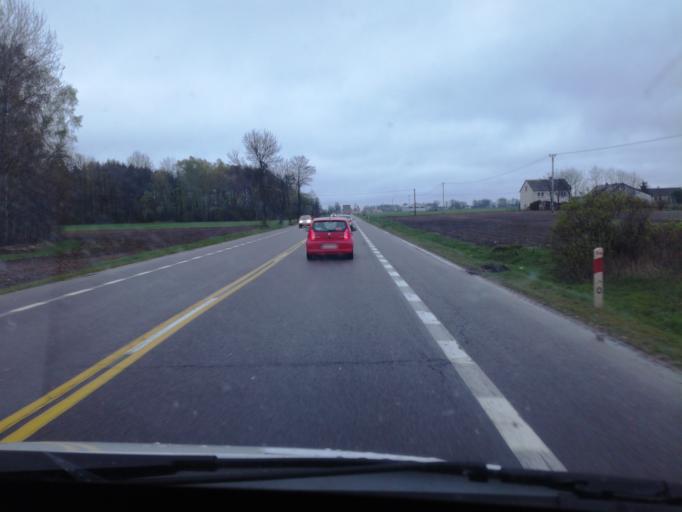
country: PL
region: Podlasie
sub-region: Powiat zambrowski
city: Szumowo
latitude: 52.9353
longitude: 22.1454
